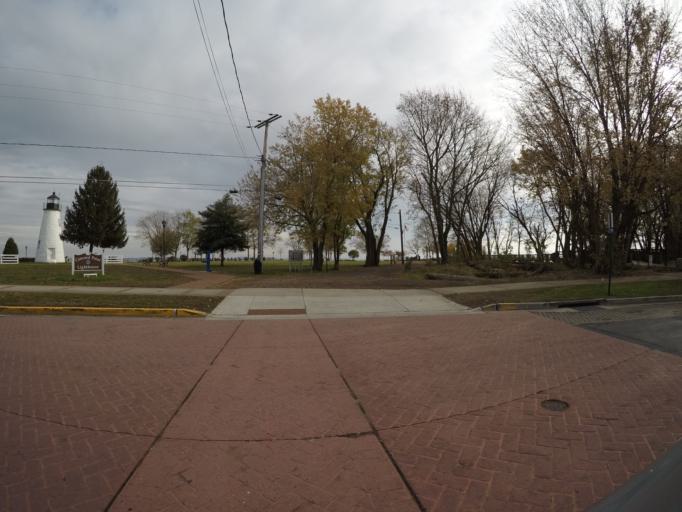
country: US
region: Maryland
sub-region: Harford County
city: Havre de Grace
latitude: 39.5407
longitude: -76.0855
